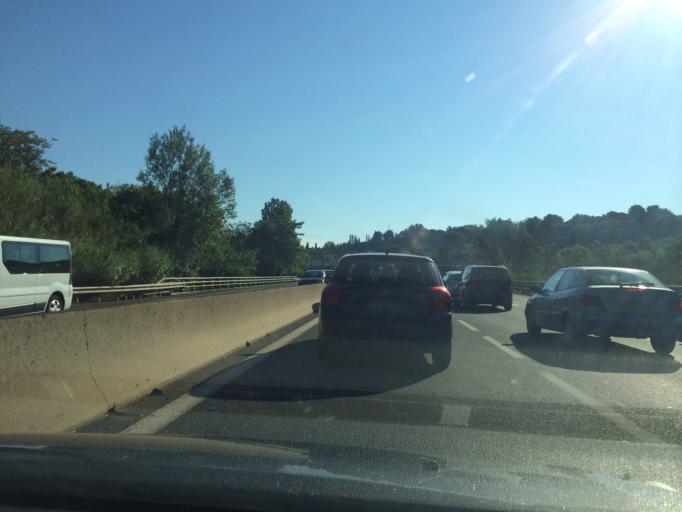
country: FR
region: Languedoc-Roussillon
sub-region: Departement de l'Herault
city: Juvignac
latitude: 43.6069
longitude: 3.8188
